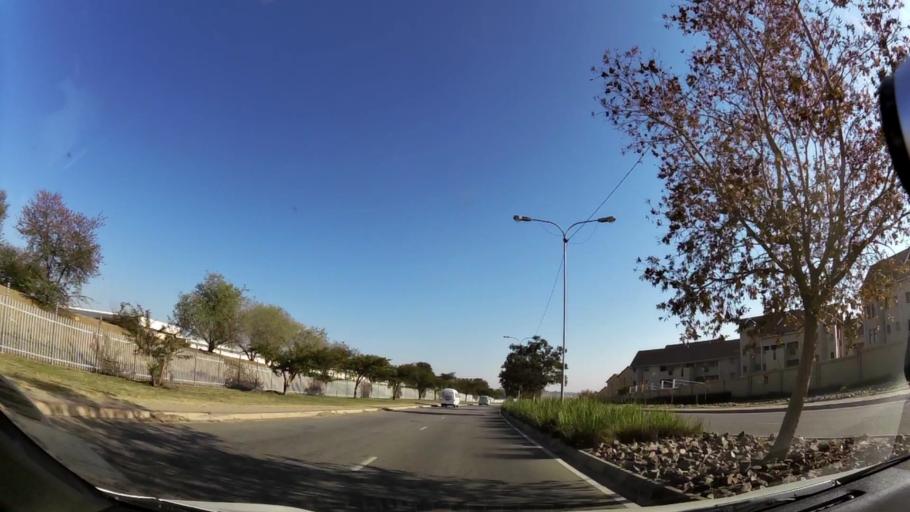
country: ZA
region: Gauteng
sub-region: City of Johannesburg Metropolitan Municipality
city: Midrand
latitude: -25.9198
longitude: 28.1288
